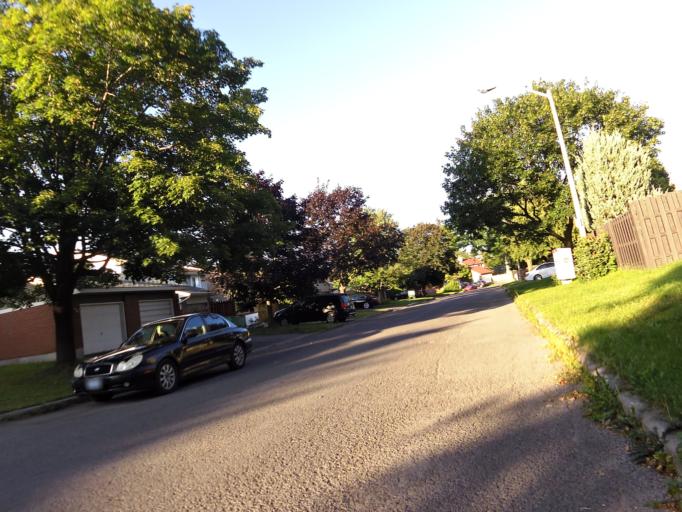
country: CA
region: Ontario
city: Ottawa
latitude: 45.3713
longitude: -75.7155
